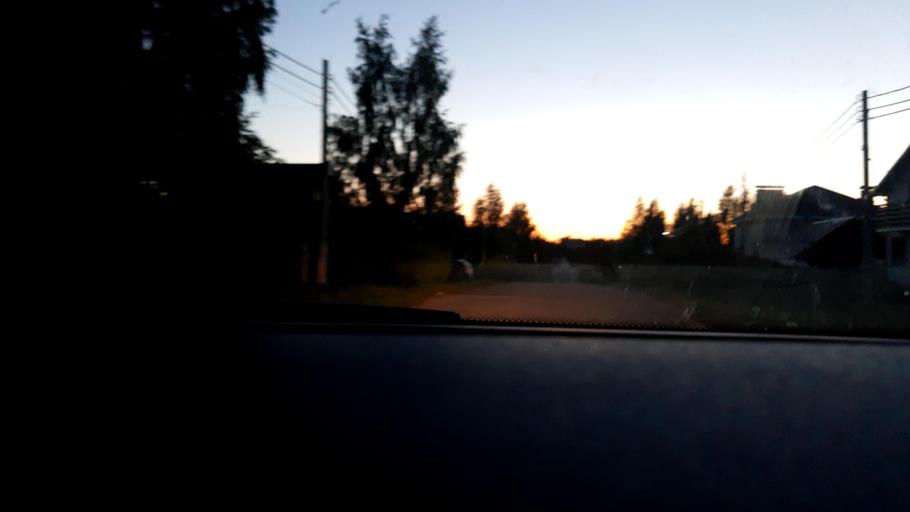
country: RU
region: Nizjnij Novgorod
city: Nizhniy Novgorod
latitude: 56.2172
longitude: 43.9539
